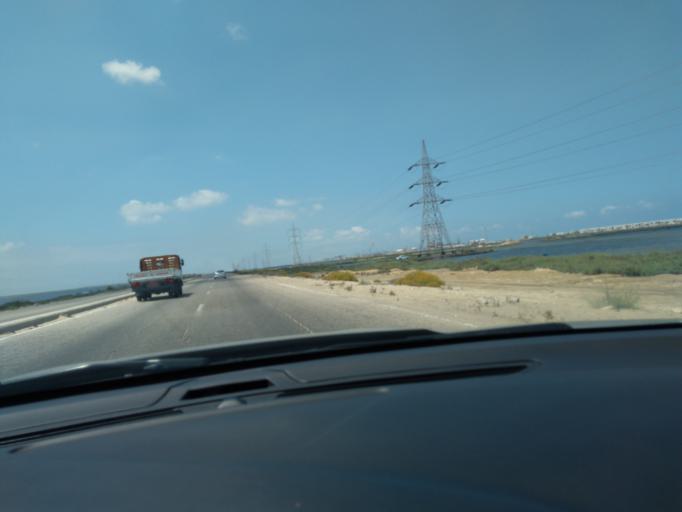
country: EG
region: Muhafazat Bur Sa`id
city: Port Said
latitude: 31.2842
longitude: 32.1830
